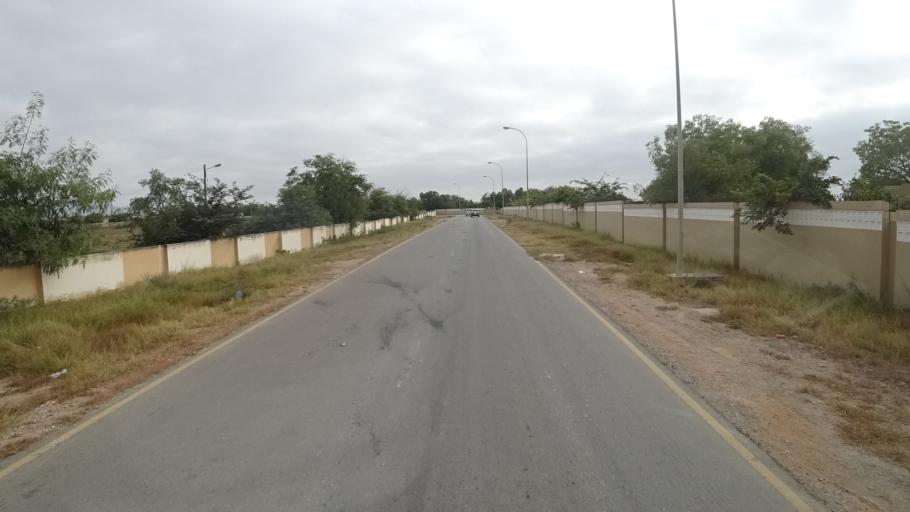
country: OM
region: Zufar
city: Salalah
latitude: 17.0062
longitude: 54.0459
